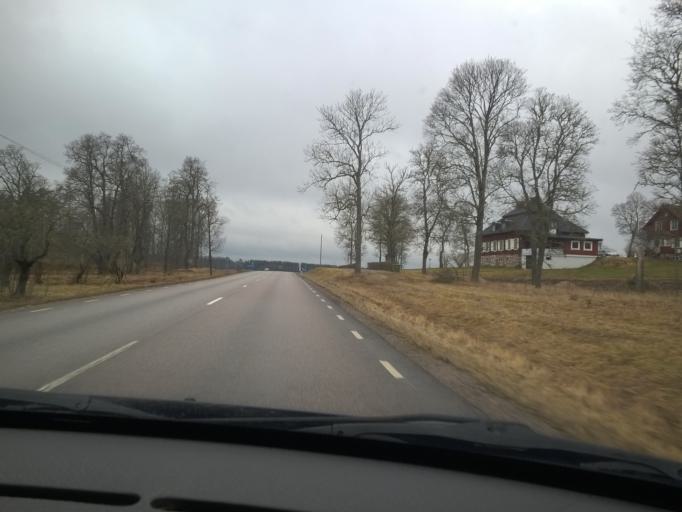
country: SE
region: Uppsala
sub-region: Tierps Kommun
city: Orbyhus
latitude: 60.1763
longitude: 17.6255
